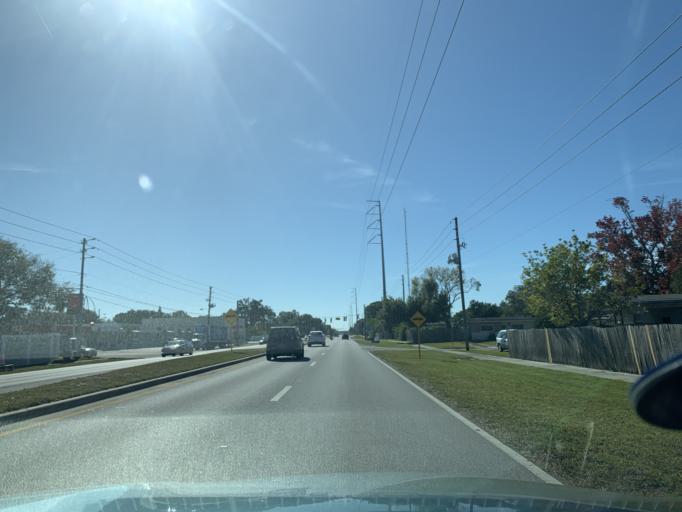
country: US
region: Florida
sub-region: Pinellas County
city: Seminole
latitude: 27.8554
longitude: -82.7624
